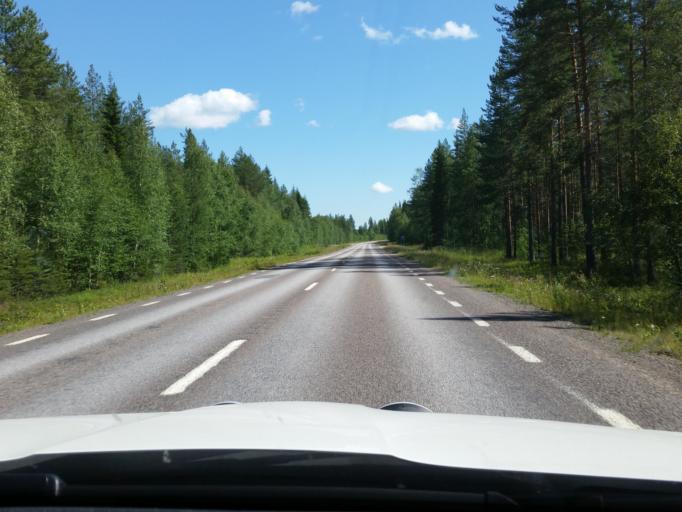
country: SE
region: Norrbotten
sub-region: Alvsbyns Kommun
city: AElvsbyn
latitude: 65.6976
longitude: 20.5249
